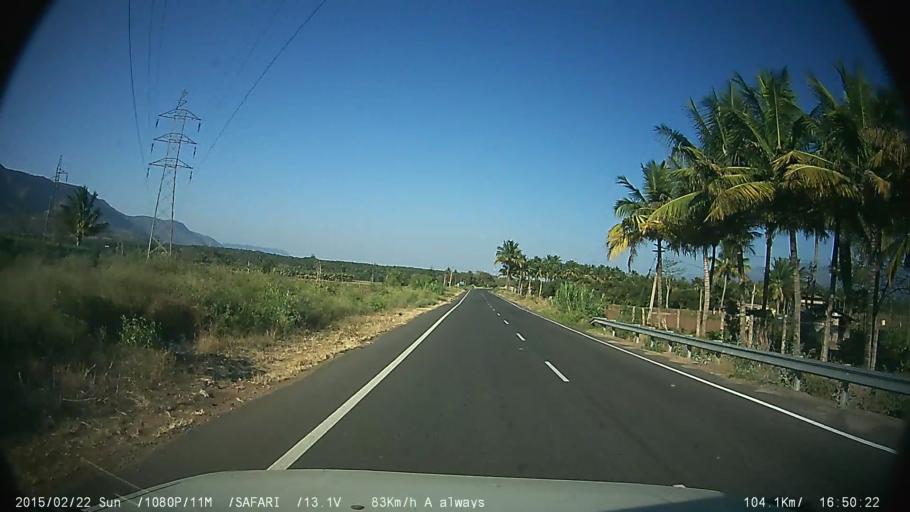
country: IN
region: Tamil Nadu
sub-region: Theni
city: Gudalur
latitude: 9.6406
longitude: 77.2092
